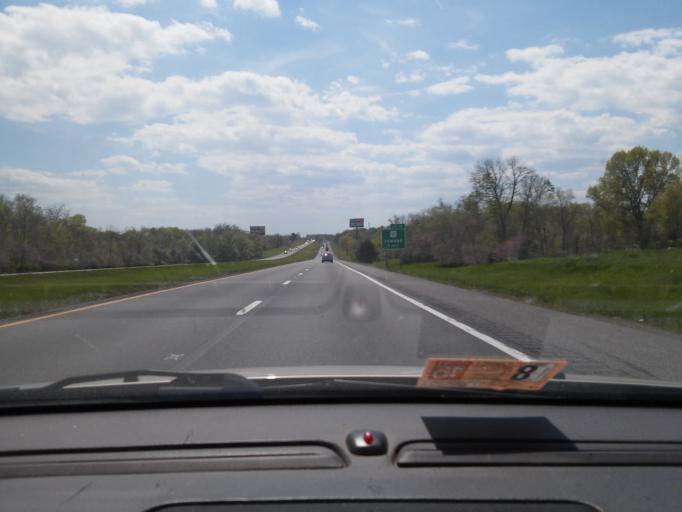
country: US
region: West Virginia
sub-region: Berkeley County
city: Inwood
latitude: 39.3770
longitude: -78.0356
